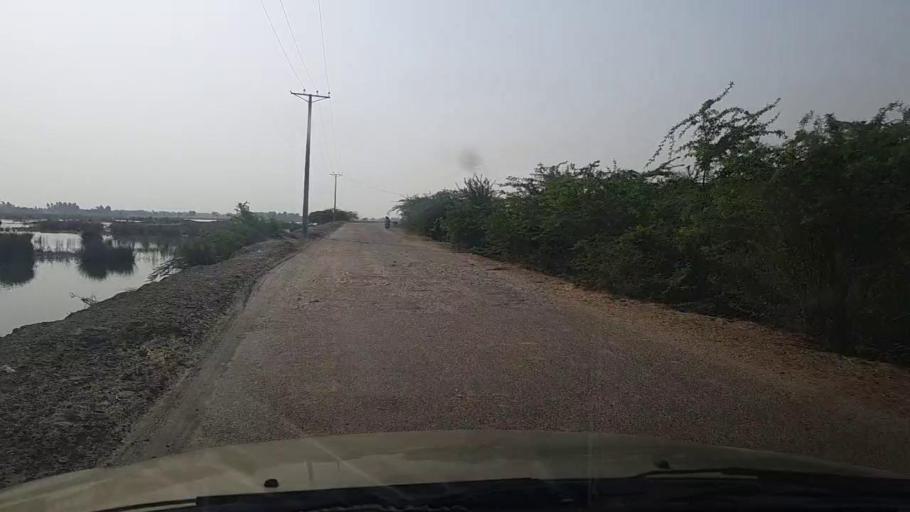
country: PK
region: Sindh
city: Kot Diji
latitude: 27.2964
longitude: 68.6420
